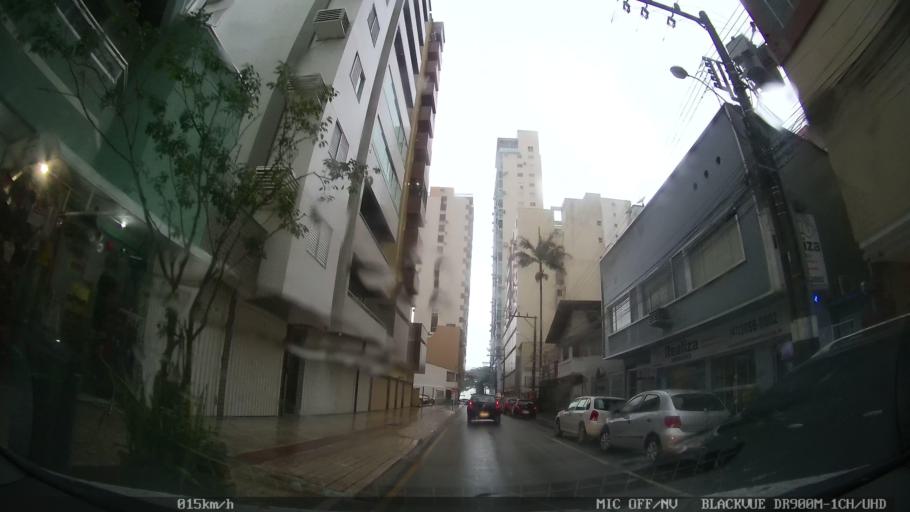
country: BR
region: Santa Catarina
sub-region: Balneario Camboriu
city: Balneario Camboriu
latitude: -26.9894
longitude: -48.6315
